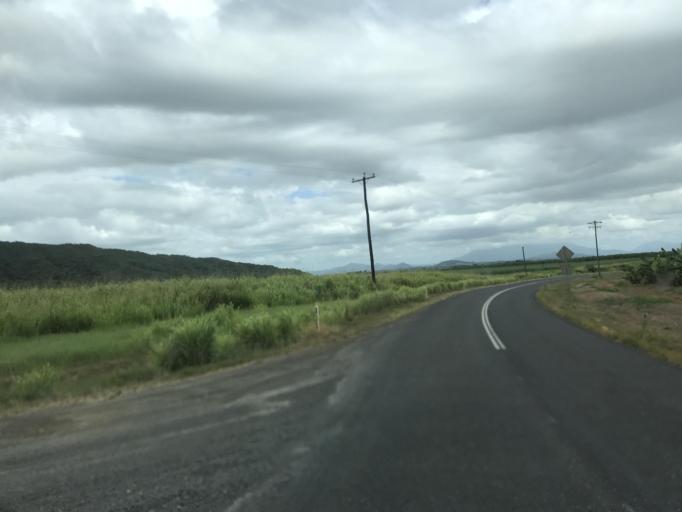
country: AU
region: Queensland
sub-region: Cassowary Coast
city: Innisfail
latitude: -17.6201
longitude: 146.0179
